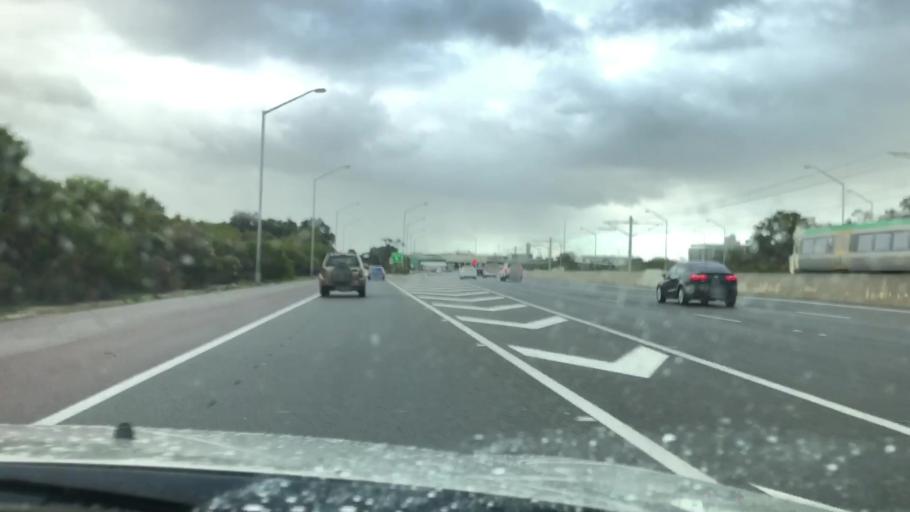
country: AU
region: Western Australia
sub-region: Melville
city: Mount Pleasant
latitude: -32.0599
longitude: 115.8514
